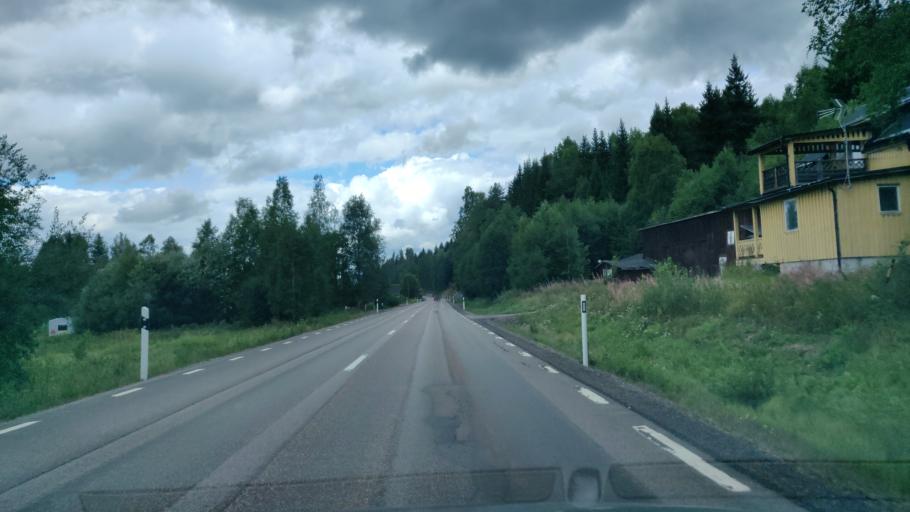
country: SE
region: Vaermland
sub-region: Torsby Kommun
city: Torsby
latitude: 60.5743
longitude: 13.0869
